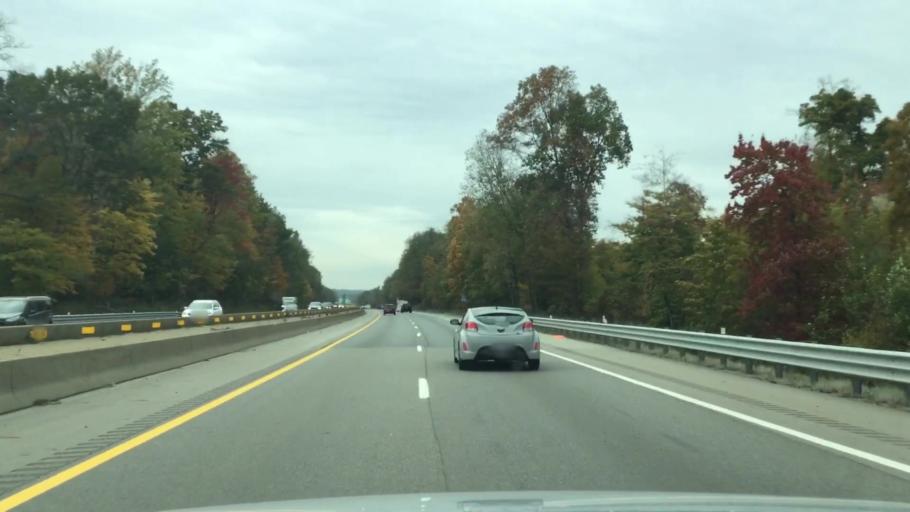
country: US
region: Michigan
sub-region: Kalamazoo County
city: Galesburg
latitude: 42.2813
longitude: -85.3842
